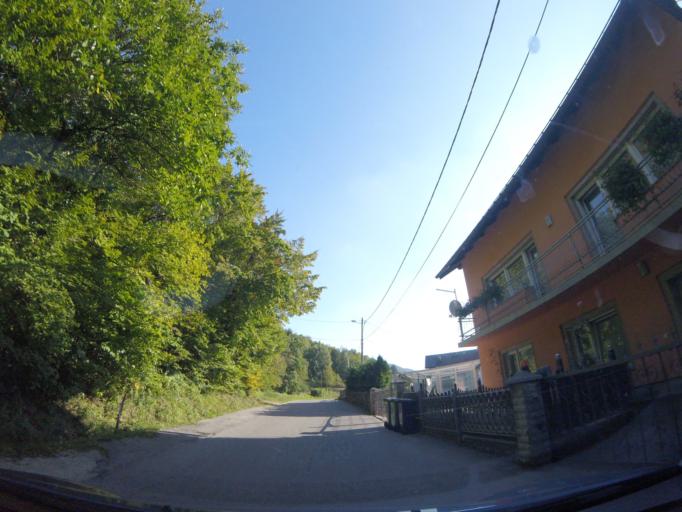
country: HR
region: Zagrebacka
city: Rude
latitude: 45.7546
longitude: 15.6738
